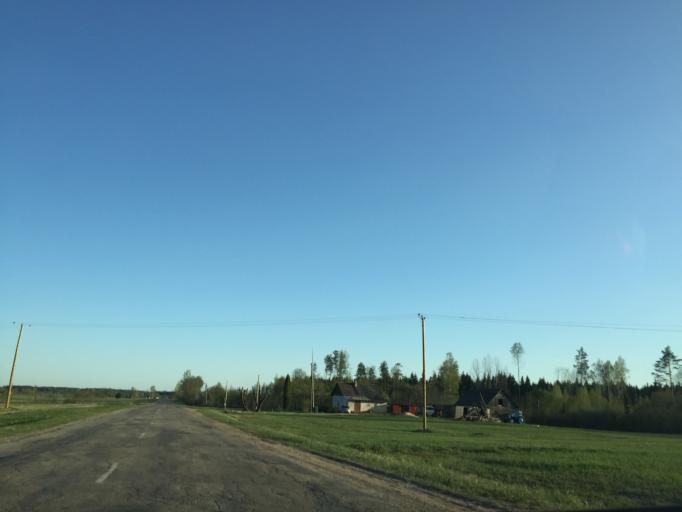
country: LV
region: Koknese
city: Koknese
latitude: 56.6933
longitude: 25.4870
